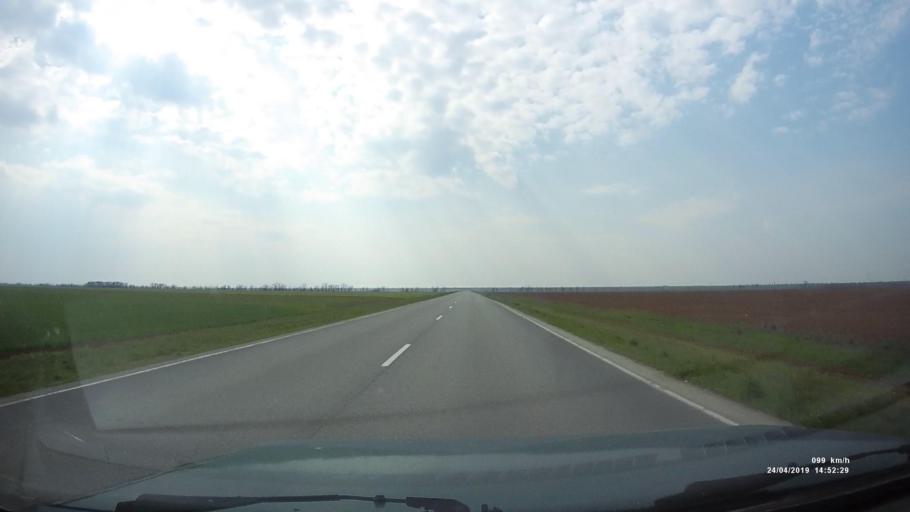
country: RU
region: Rostov
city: Remontnoye
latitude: 46.5303
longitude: 43.6796
